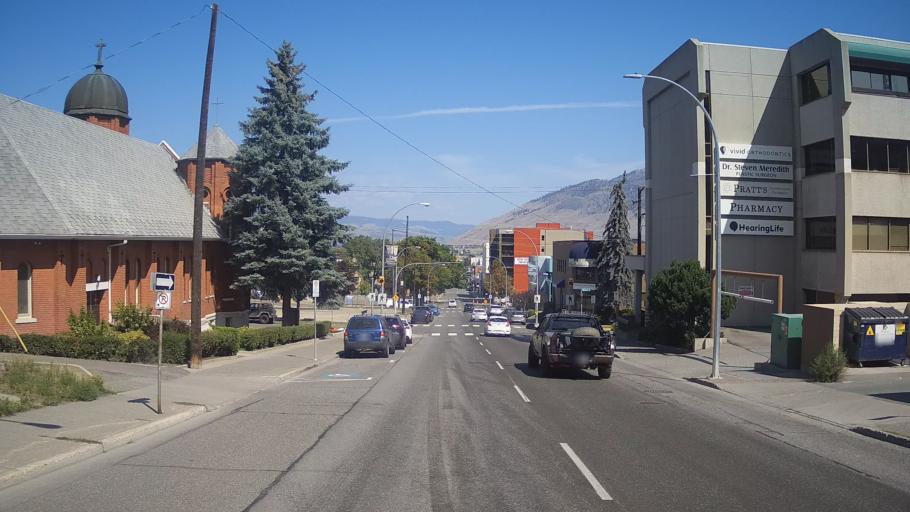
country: CA
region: British Columbia
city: Kamloops
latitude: 50.6718
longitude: -120.3345
